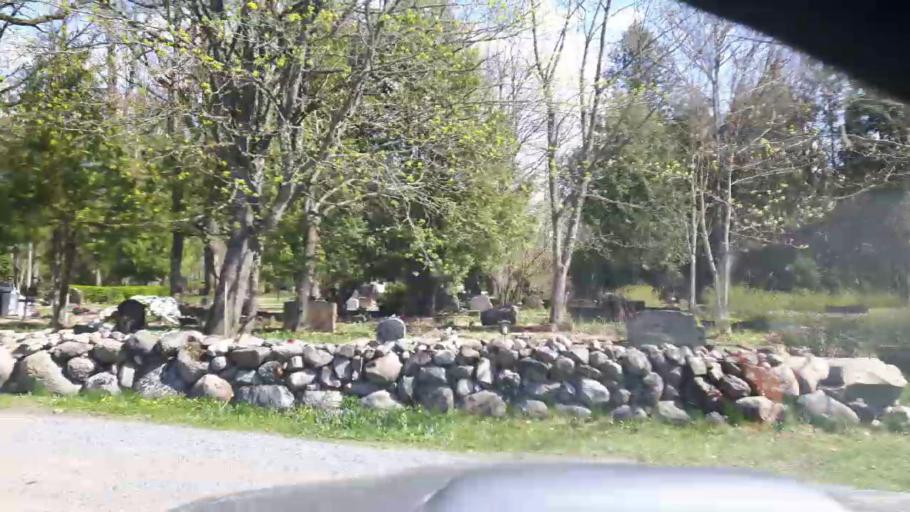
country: EE
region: Paernumaa
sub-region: Tootsi vald
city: Tootsi
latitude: 58.4827
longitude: 24.8171
